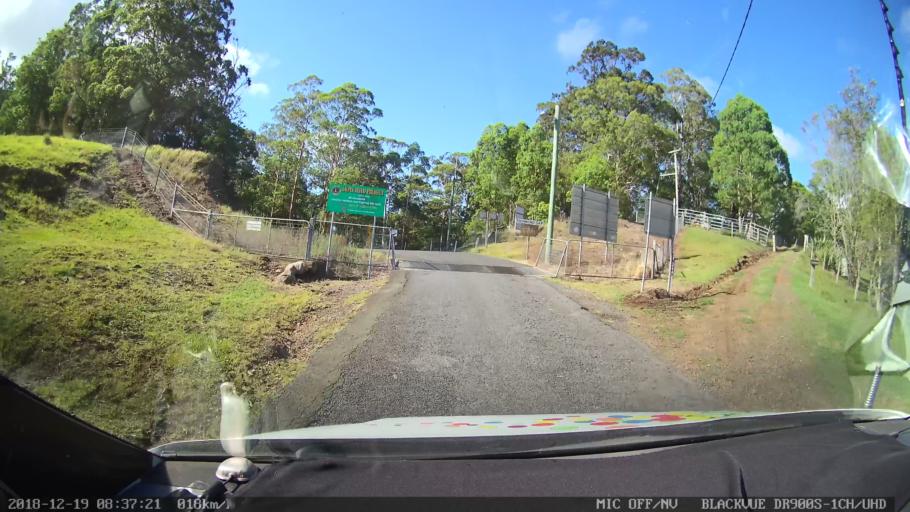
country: AU
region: New South Wales
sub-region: Kyogle
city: Kyogle
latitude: -28.3315
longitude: 152.9731
